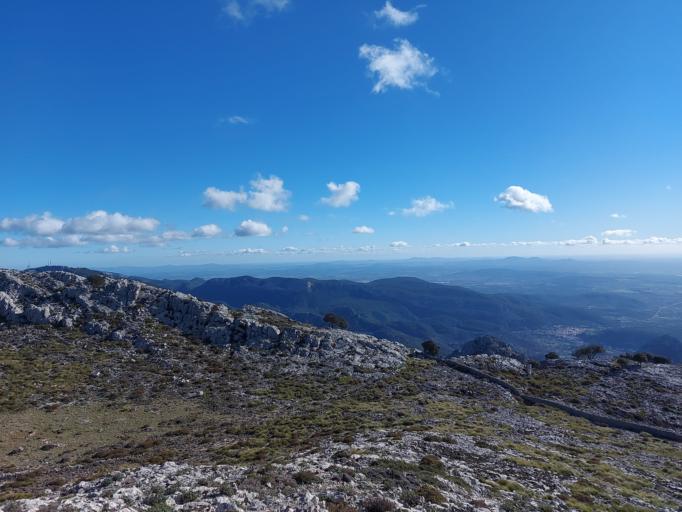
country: ES
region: Balearic Islands
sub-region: Illes Balears
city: Deia
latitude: 39.7313
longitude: 2.6613
